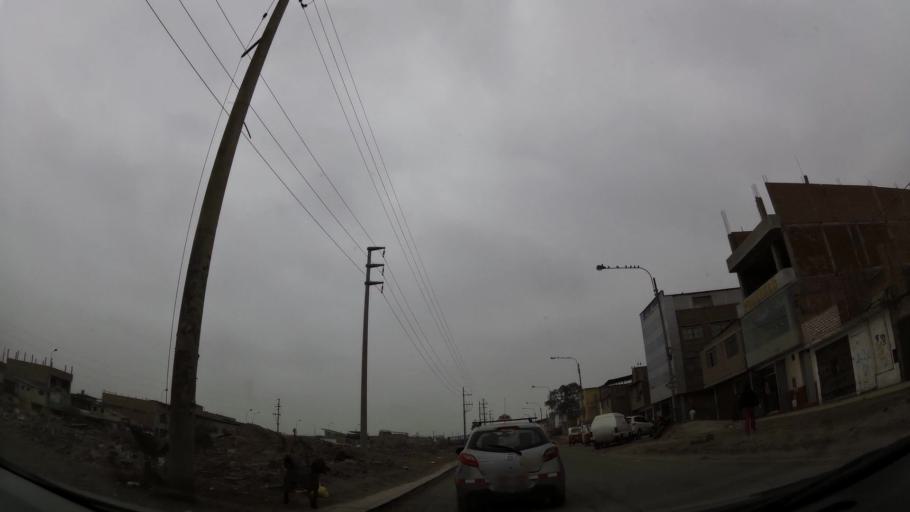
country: PE
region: Lima
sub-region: Lima
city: Surco
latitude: -12.2190
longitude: -76.9262
